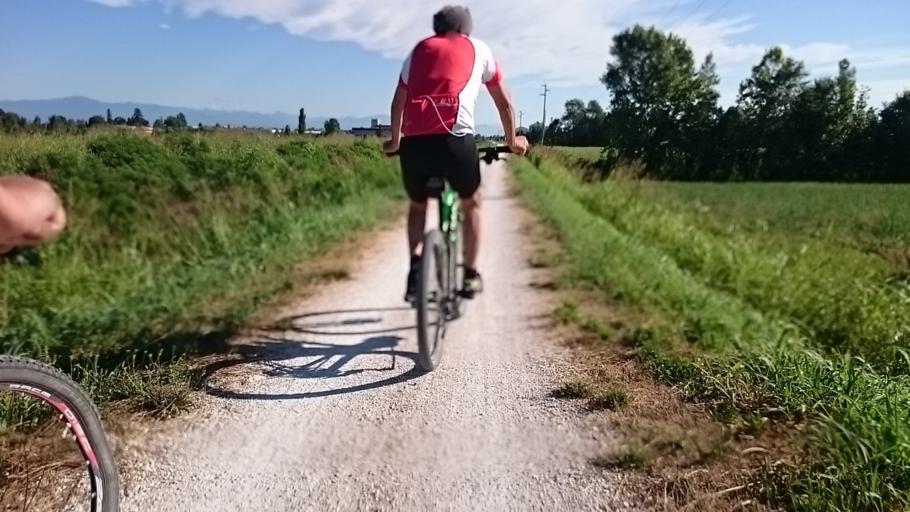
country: IT
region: Veneto
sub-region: Provincia di Padova
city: Borgoricco-San Michele delle Badesse-Sant'Eufemia
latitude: 45.5317
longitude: 11.9232
